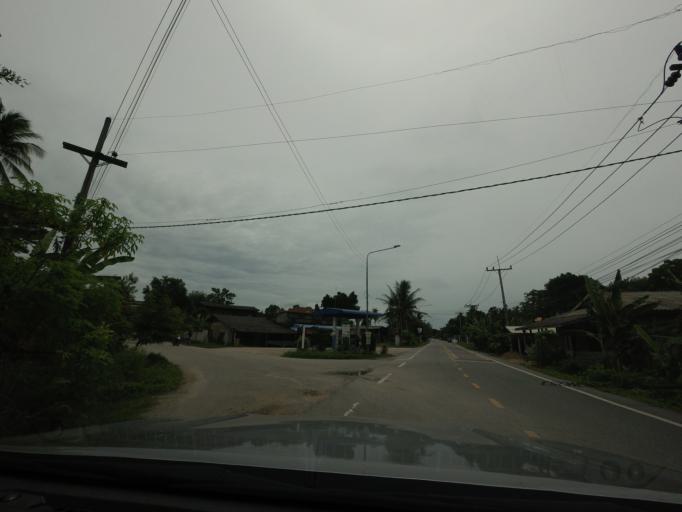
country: TH
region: Pattani
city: Sai Buri
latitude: 6.6517
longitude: 101.5544
